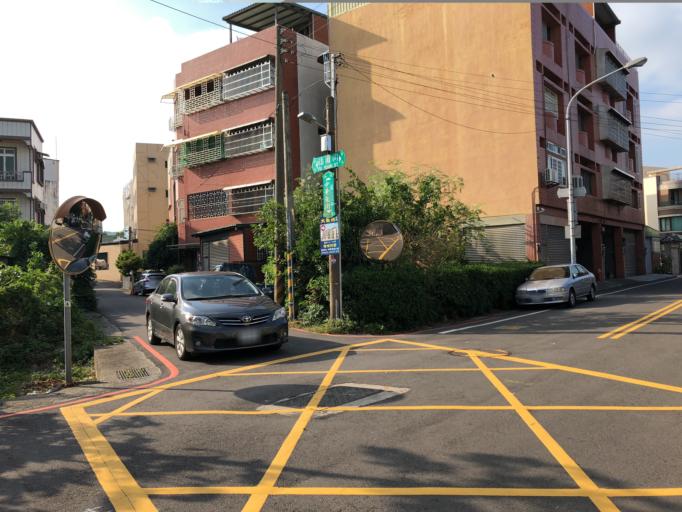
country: TW
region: Taiwan
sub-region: Miaoli
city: Miaoli
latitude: 24.5779
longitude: 120.8253
